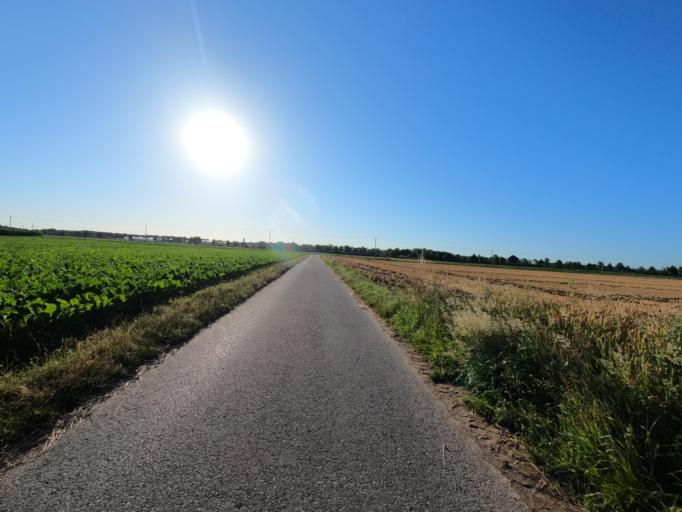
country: DE
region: North Rhine-Westphalia
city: Geilenkirchen
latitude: 50.9824
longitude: 6.0893
